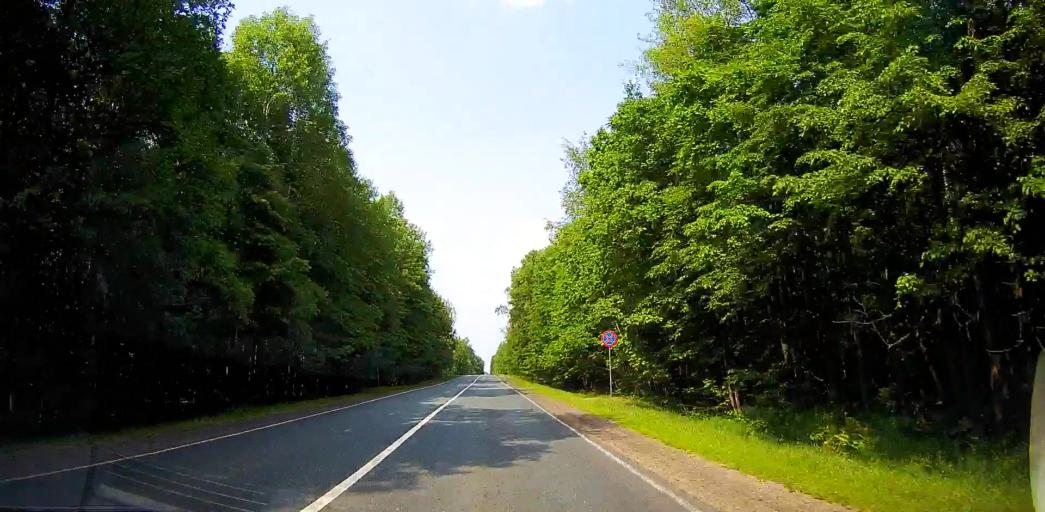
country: RU
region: Moskovskaya
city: Malino
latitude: 54.9914
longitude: 38.1688
